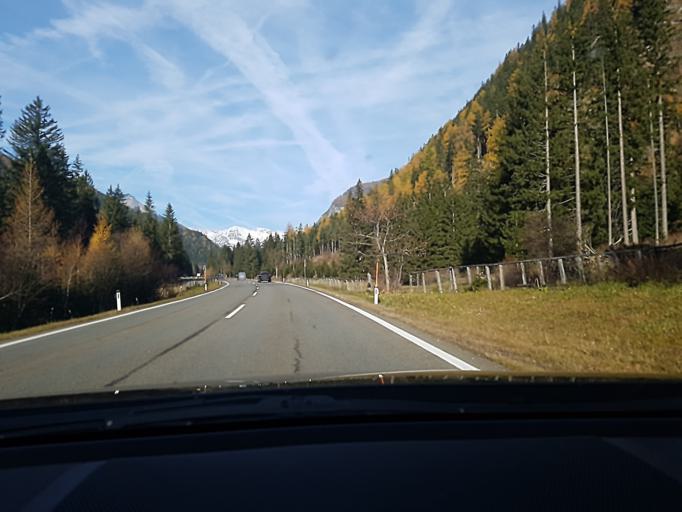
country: AT
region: Salzburg
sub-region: Politischer Bezirk Tamsweg
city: Tweng
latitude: 47.1693
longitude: 13.6427
